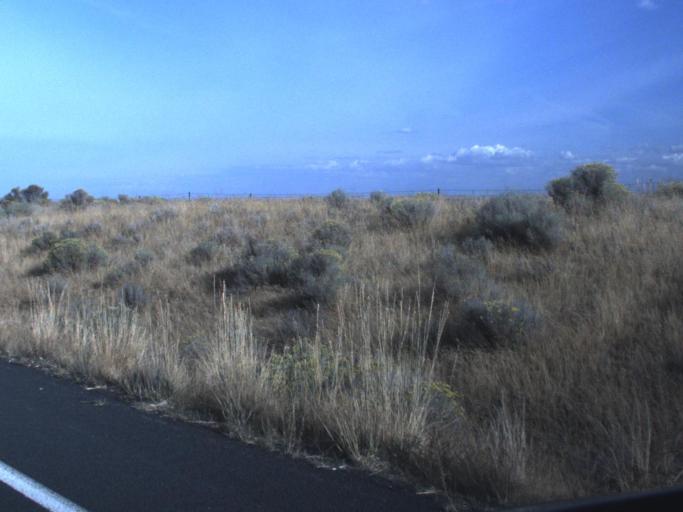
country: US
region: Oregon
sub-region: Morrow County
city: Boardman
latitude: 45.9146
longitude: -119.6599
